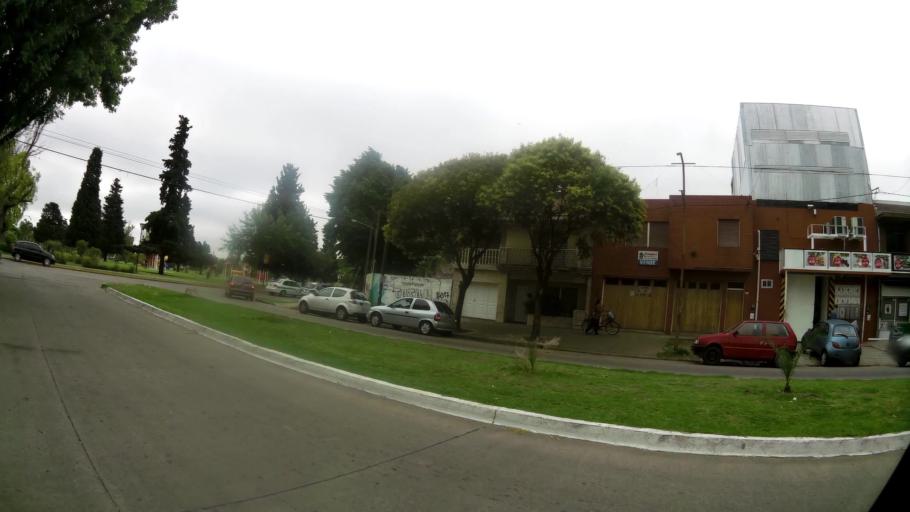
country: AR
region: Buenos Aires
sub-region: Partido de La Plata
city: La Plata
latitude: -34.9236
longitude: -57.9792
